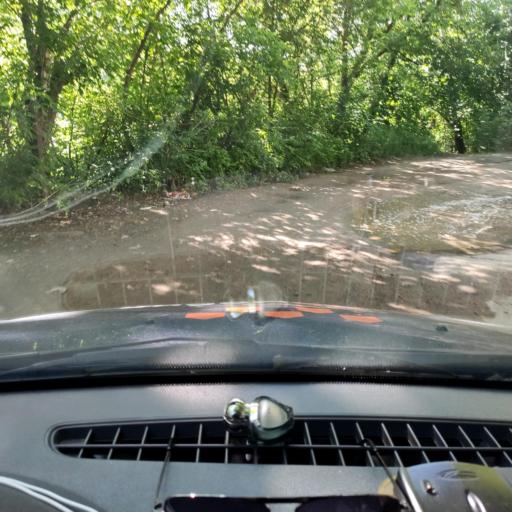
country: RU
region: Orjol
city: Orel
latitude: 52.9848
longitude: 36.0405
